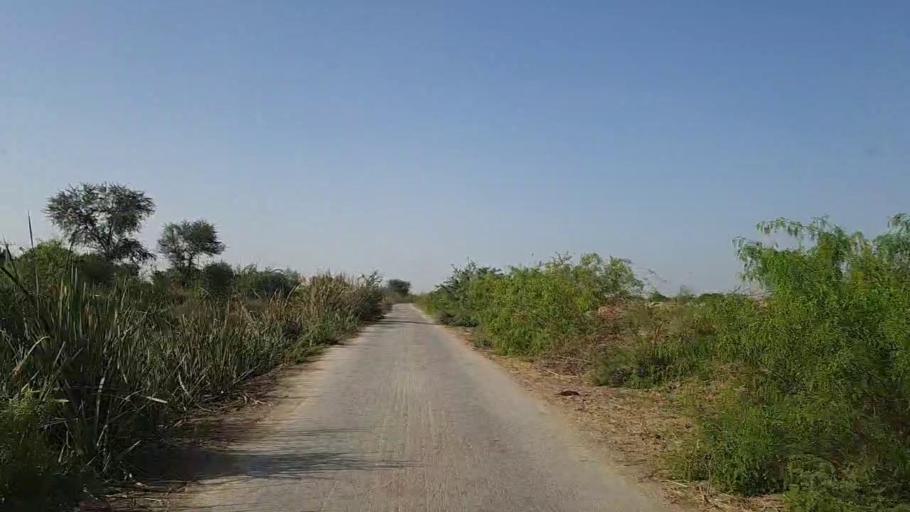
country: PK
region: Sindh
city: Kotri
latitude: 25.1557
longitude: 68.2644
